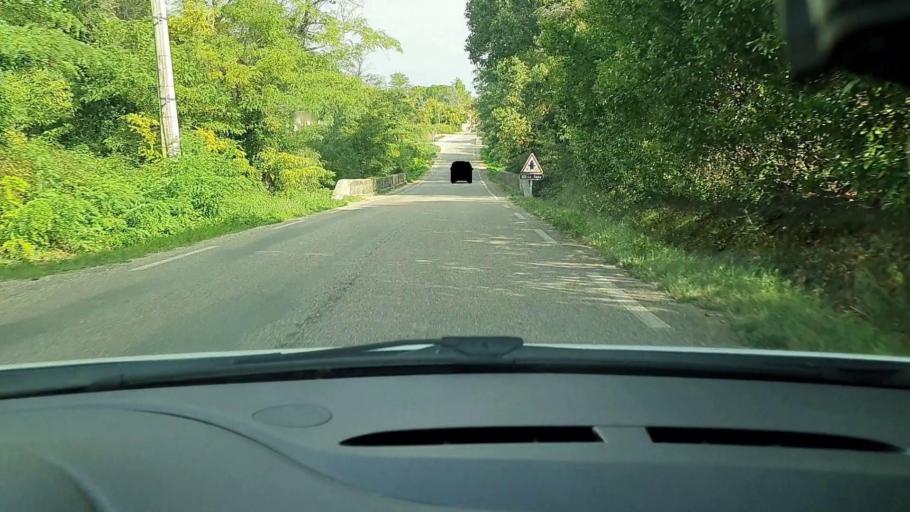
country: FR
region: Languedoc-Roussillon
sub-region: Departement du Gard
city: Saint-Quentin-la-Poterie
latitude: 44.1000
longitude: 4.4544
